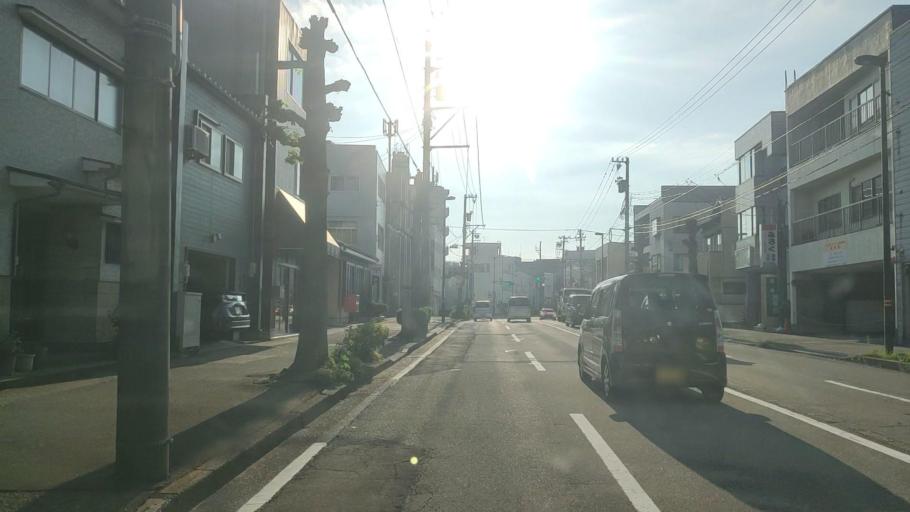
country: JP
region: Ishikawa
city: Kanazawa-shi
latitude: 36.5636
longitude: 136.6689
